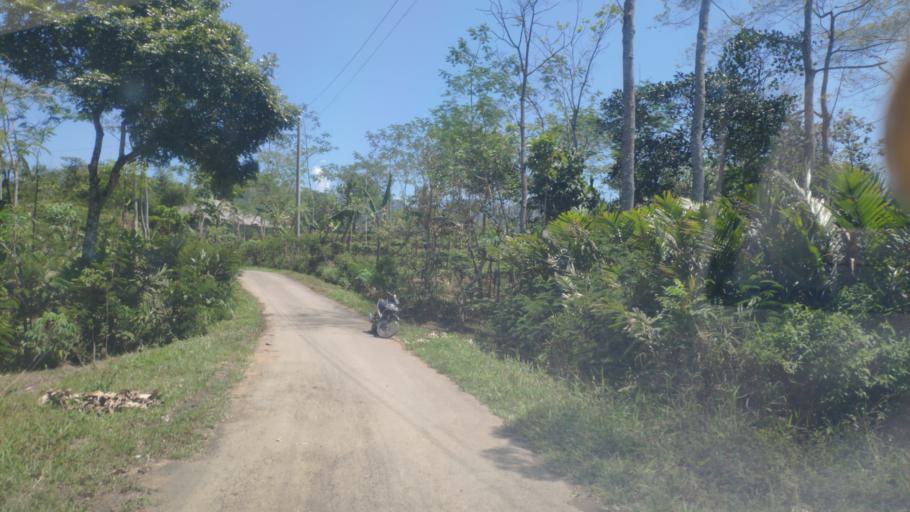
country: ID
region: Central Java
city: Buaran
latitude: -7.2591
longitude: 109.6543
